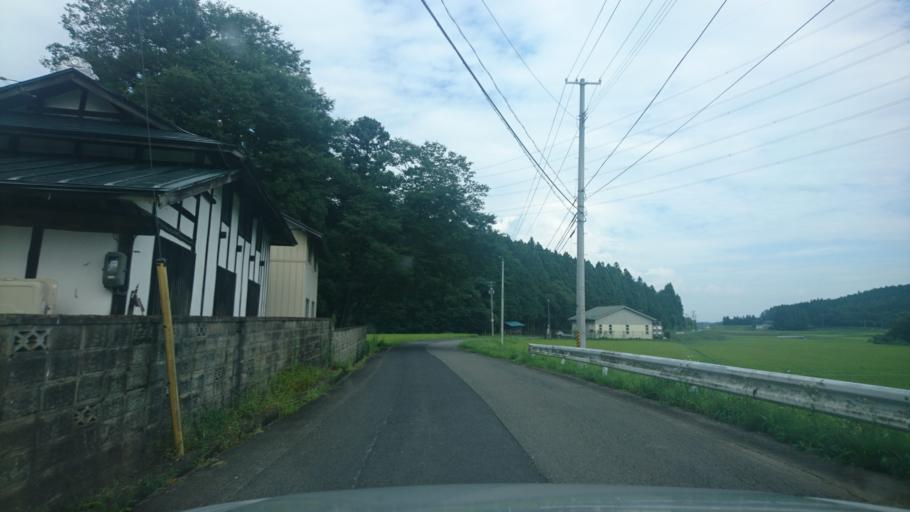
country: JP
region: Miyagi
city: Furukawa
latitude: 38.7727
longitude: 140.9260
